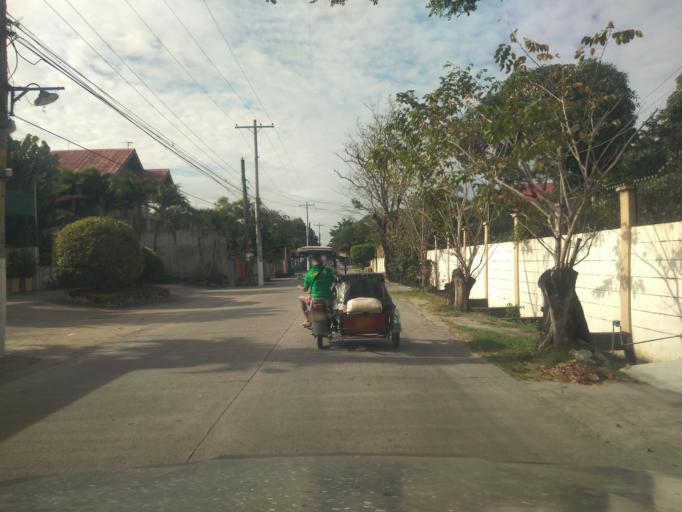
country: PH
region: Central Luzon
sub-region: Province of Pampanga
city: Sexmoan
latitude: 14.9530
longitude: 120.6283
